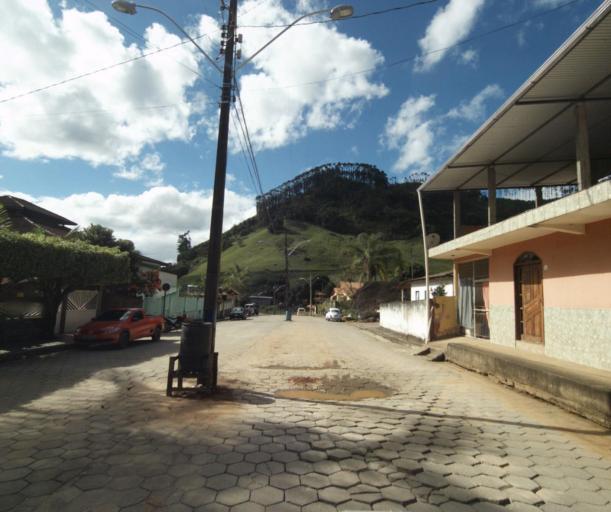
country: BR
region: Espirito Santo
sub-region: Irupi
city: Irupi
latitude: -20.5323
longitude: -41.6670
